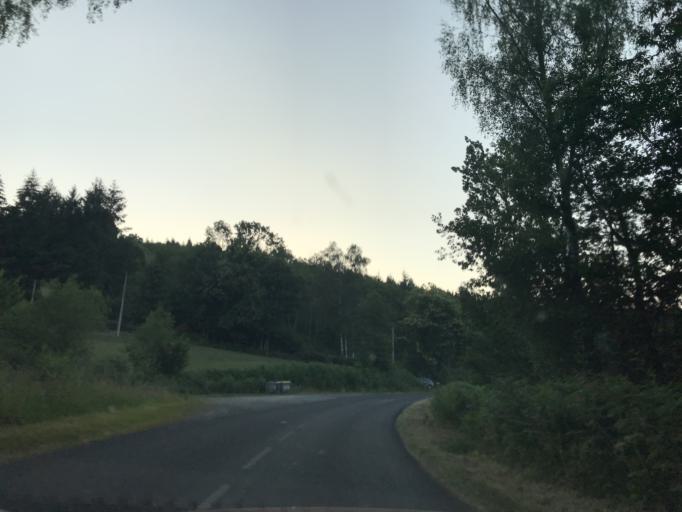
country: FR
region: Auvergne
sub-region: Departement du Puy-de-Dome
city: Celles-sur-Durolle
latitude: 45.7494
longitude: 3.6566
